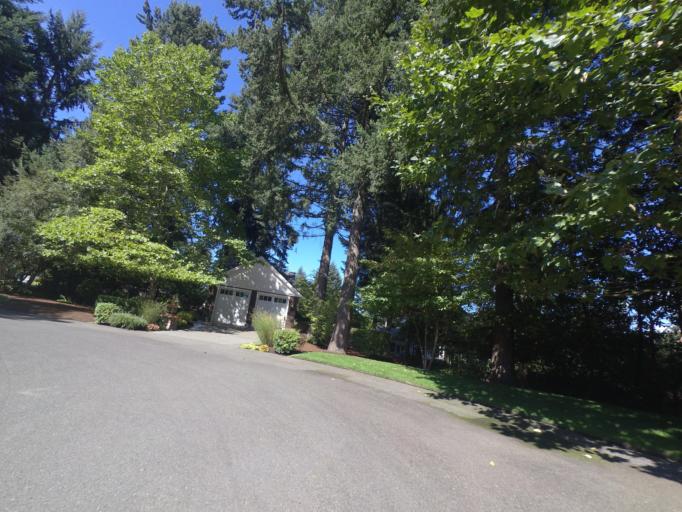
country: US
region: Washington
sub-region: Pierce County
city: Fircrest
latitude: 47.2132
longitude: -122.5199
